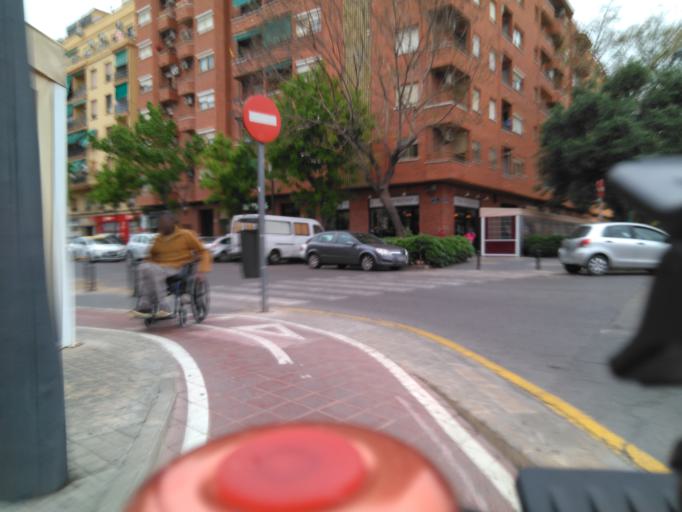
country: ES
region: Valencia
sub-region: Provincia de Valencia
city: Mislata
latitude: 39.4703
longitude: -0.3990
